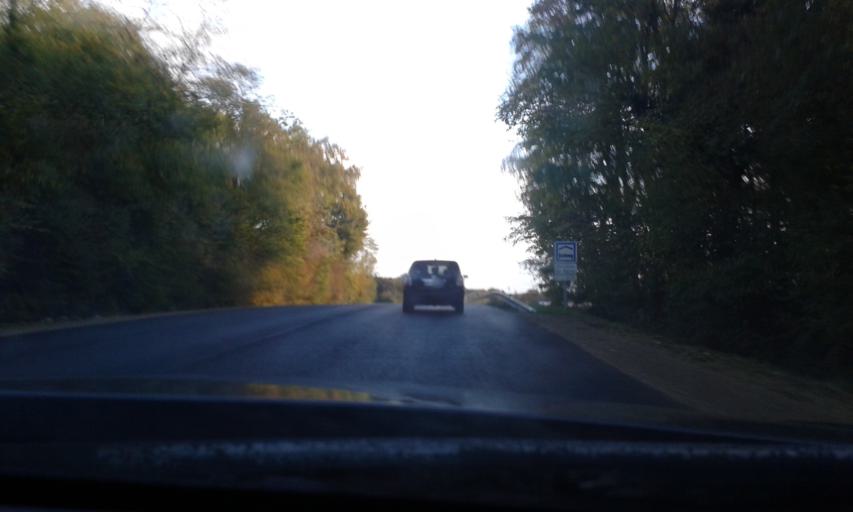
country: FR
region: Centre
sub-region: Departement d'Eure-et-Loir
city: Sours
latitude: 48.3955
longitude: 1.5621
